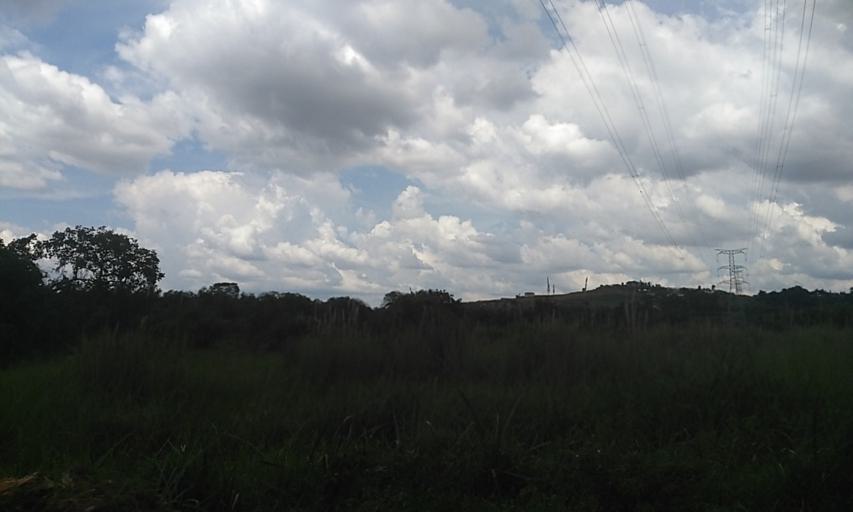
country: UG
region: Central Region
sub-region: Wakiso District
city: Wakiso
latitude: 0.3507
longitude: 32.4764
